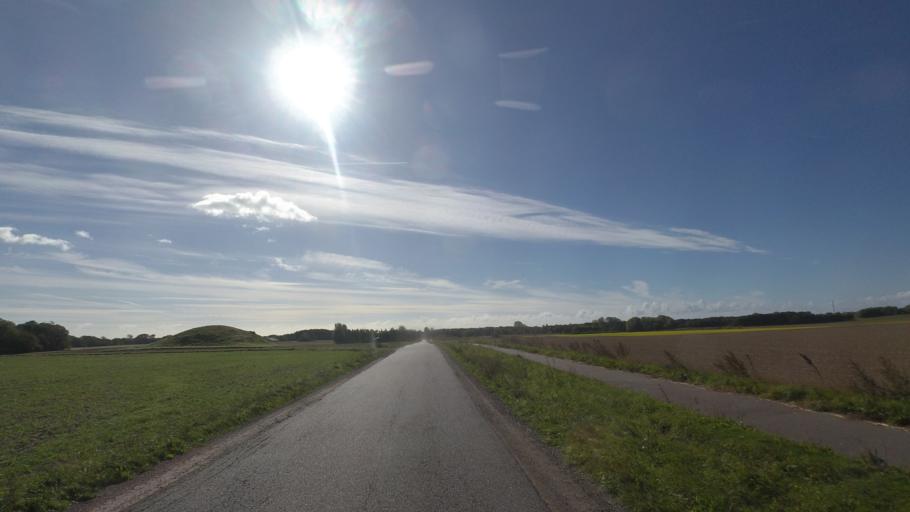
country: DK
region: Capital Region
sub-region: Bornholm Kommune
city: Akirkeby
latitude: 55.0180
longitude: 14.9926
